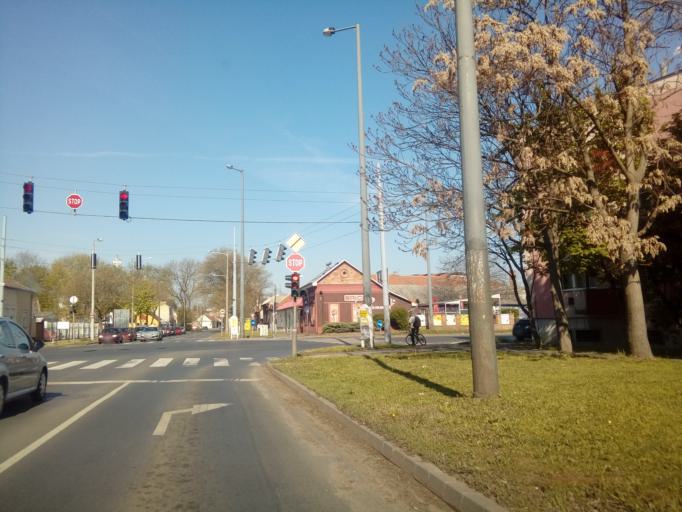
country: HU
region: Szabolcs-Szatmar-Bereg
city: Nyiregyhaza
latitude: 47.9507
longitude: 21.7276
